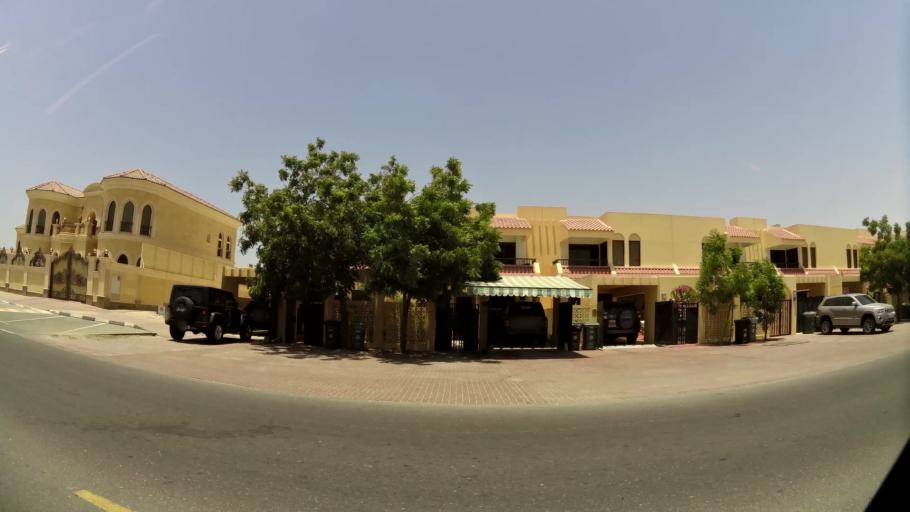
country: AE
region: Dubai
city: Dubai
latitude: 25.2255
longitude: 55.2632
